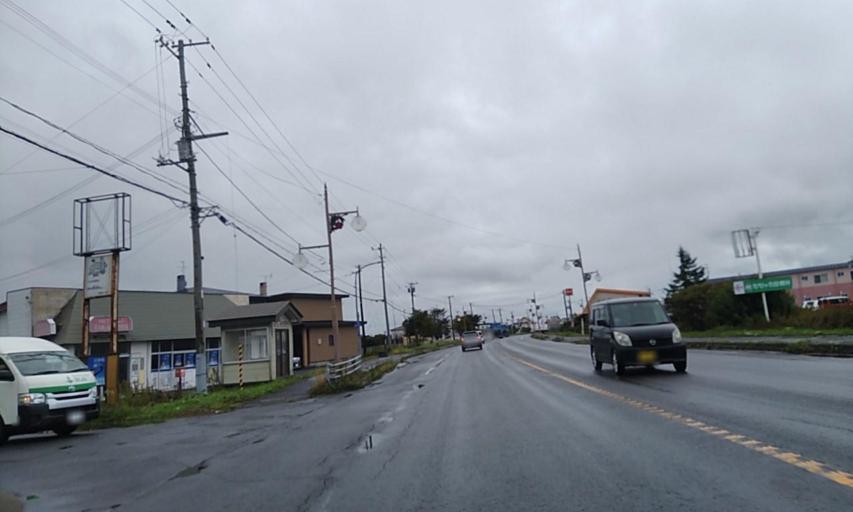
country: JP
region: Hokkaido
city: Kushiro
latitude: 42.9750
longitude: 144.1307
